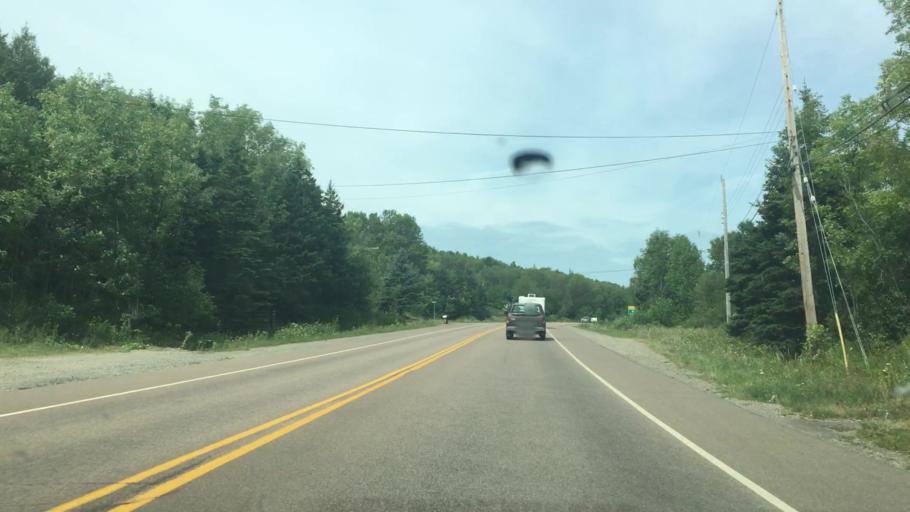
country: CA
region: Nova Scotia
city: Port Hawkesbury
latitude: 45.6544
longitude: -61.4470
